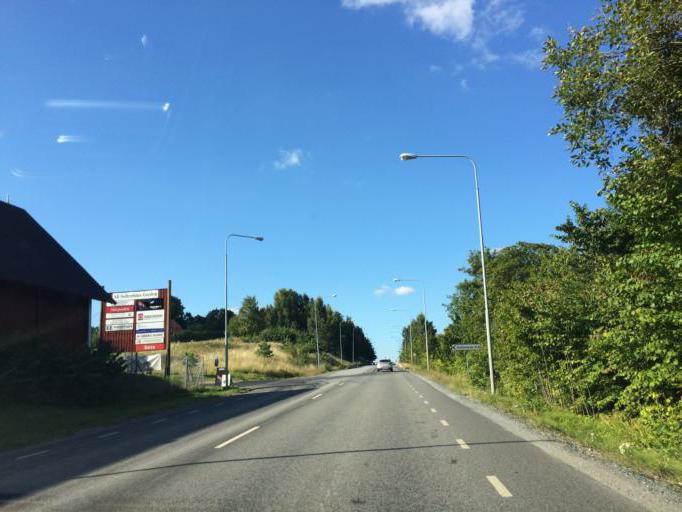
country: SE
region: Stockholm
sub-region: Sollentuna Kommun
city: Sollentuna
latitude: 59.4662
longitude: 17.9215
